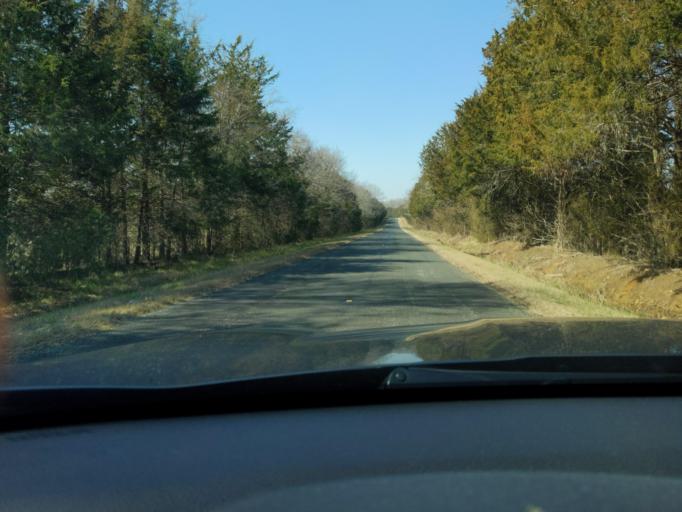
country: US
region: South Carolina
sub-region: Abbeville County
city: Calhoun Falls
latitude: 34.0855
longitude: -82.5470
